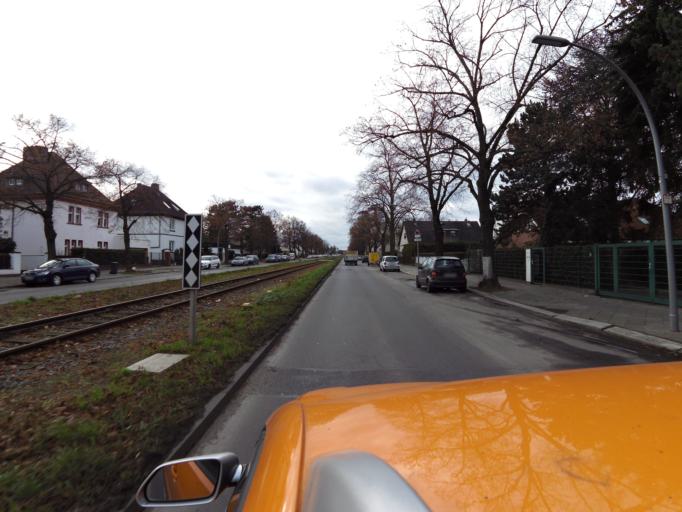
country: DE
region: Berlin
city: Rudow
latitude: 52.4269
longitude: 13.4890
